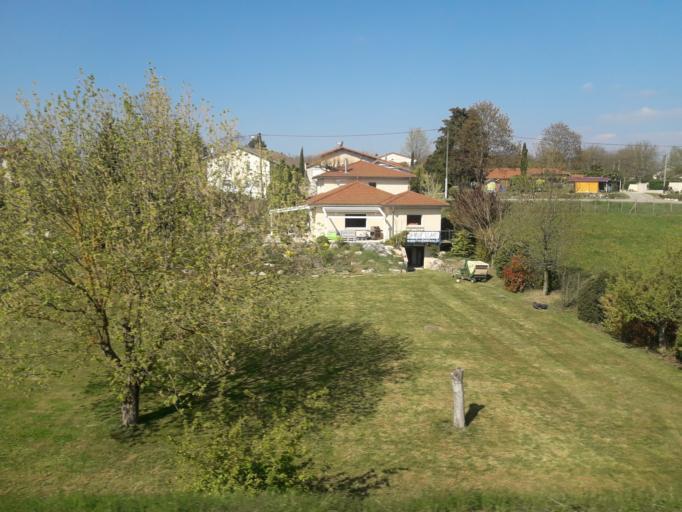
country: FR
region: Rhone-Alpes
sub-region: Departement de l'Isere
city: Saint-Hilaire-du-Rosier
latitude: 45.0720
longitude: 5.2394
